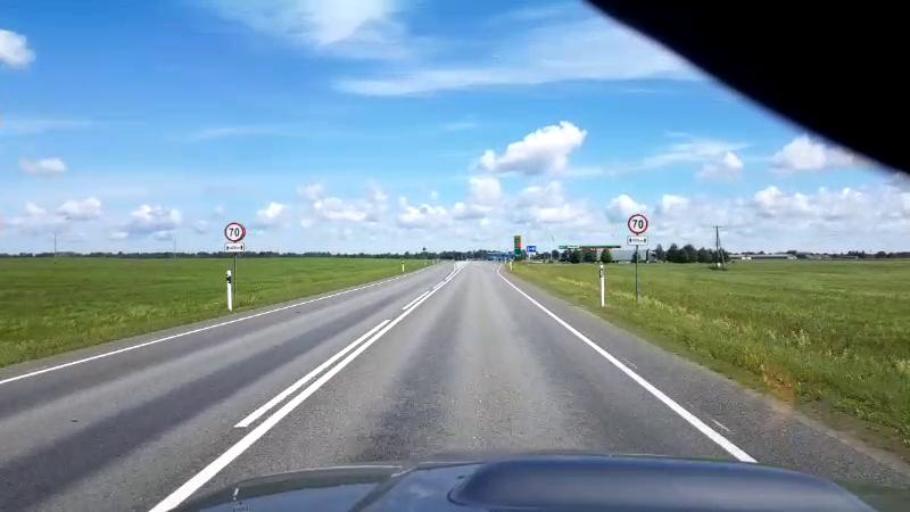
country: EE
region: Jaervamaa
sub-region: Jaerva-Jaani vald
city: Jarva-Jaani
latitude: 59.1772
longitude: 25.7595
